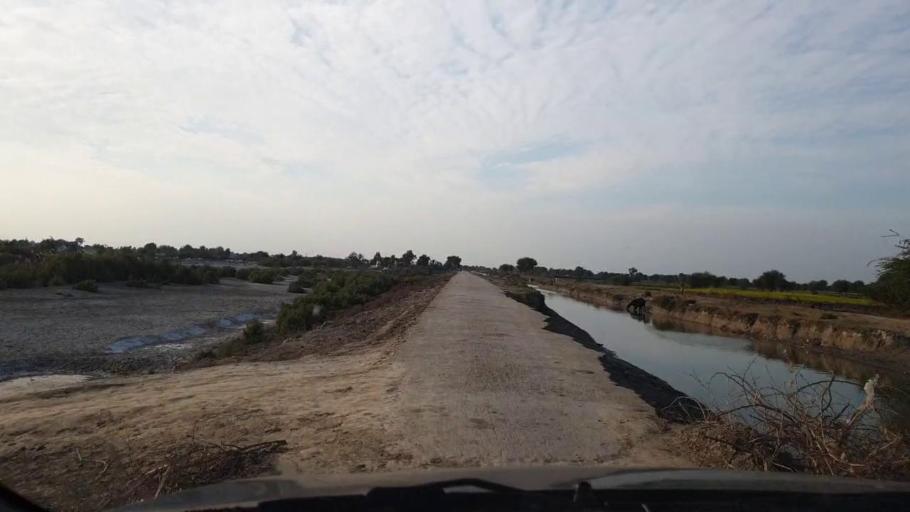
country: PK
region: Sindh
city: Jhol
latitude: 25.9524
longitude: 68.8537
